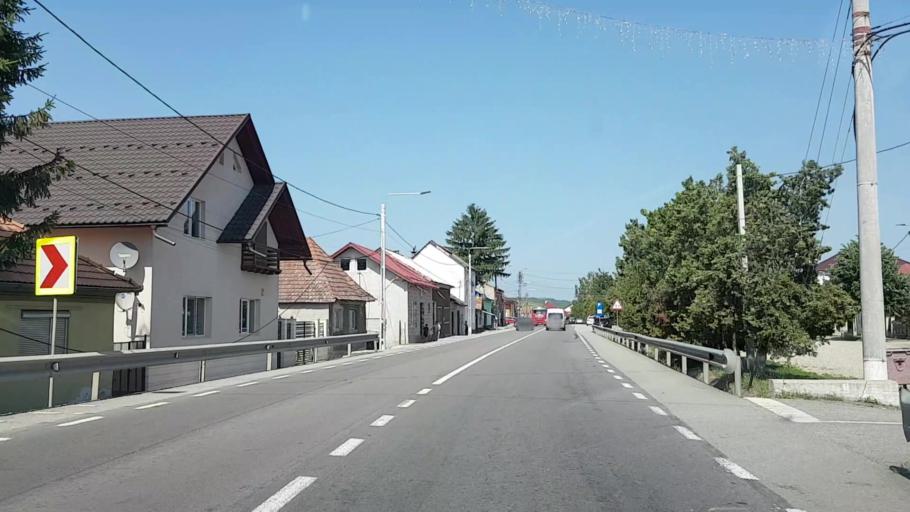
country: RO
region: Bistrita-Nasaud
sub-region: Comuna Petru Rares
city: Reteag
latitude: 47.1947
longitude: 24.0152
